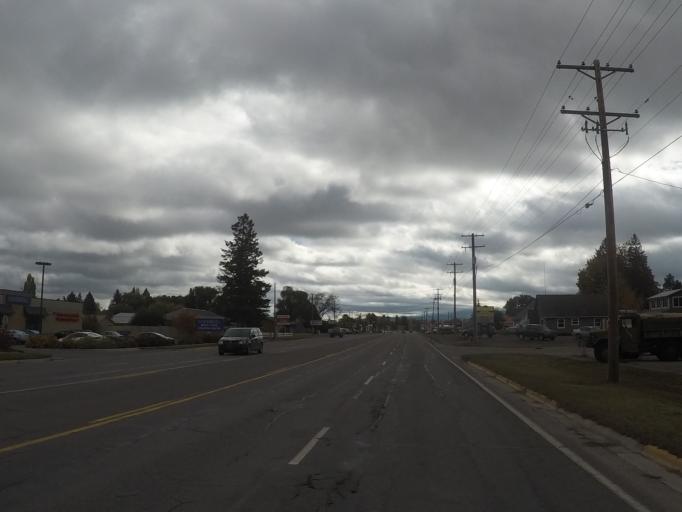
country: US
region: Montana
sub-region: Flathead County
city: Evergreen
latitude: 48.2217
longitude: -114.2774
